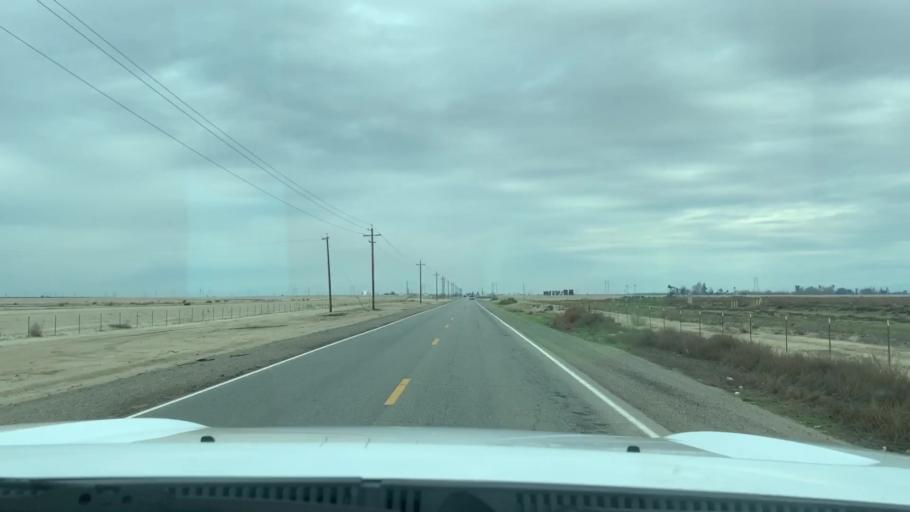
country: US
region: California
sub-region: Kern County
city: Rosedale
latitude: 35.3430
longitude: -119.2522
